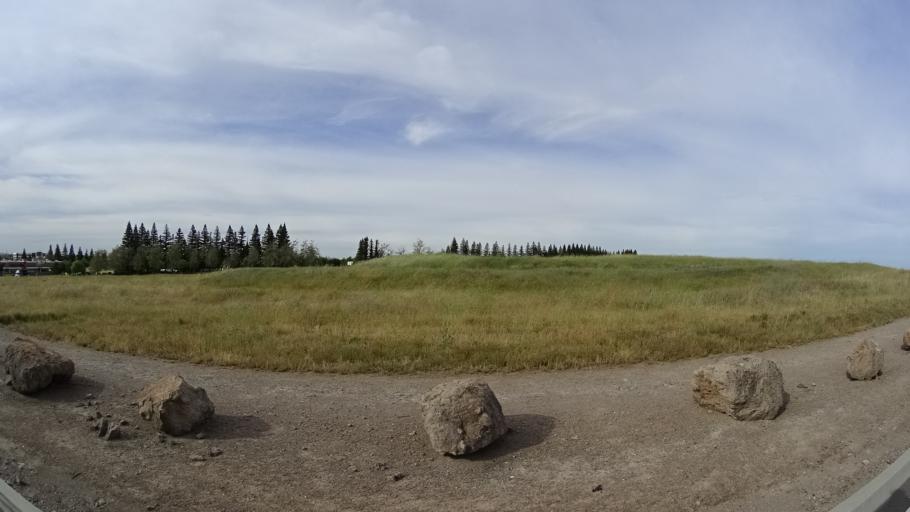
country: US
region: California
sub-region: Placer County
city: Rocklin
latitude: 38.8190
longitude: -121.2917
